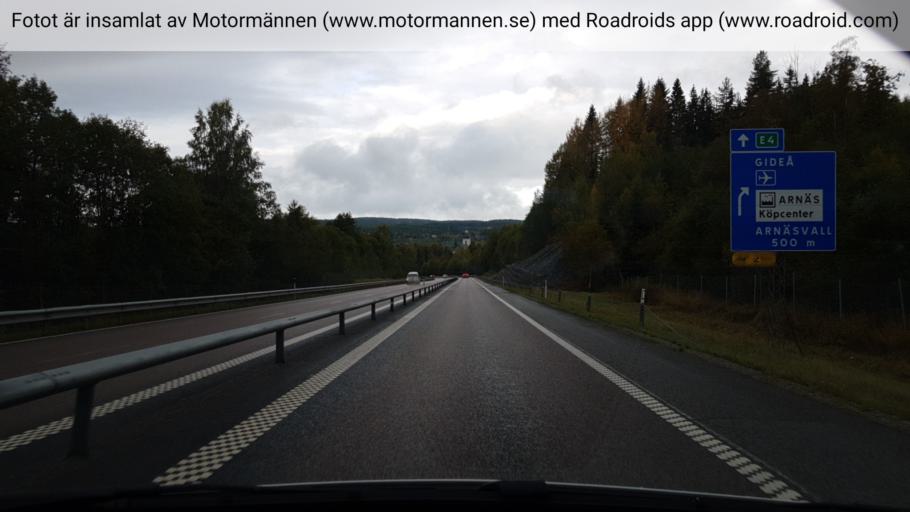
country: SE
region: Vaesternorrland
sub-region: OErnskoeldsviks Kommun
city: Ornskoldsvik
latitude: 63.3153
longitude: 18.8093
